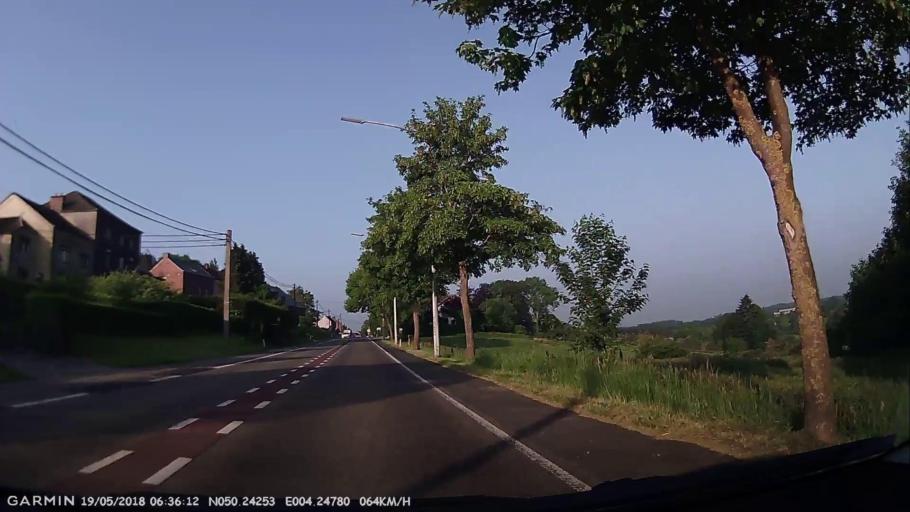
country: BE
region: Wallonia
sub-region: Province du Hainaut
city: Beaumont
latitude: 50.2424
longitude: 4.2477
